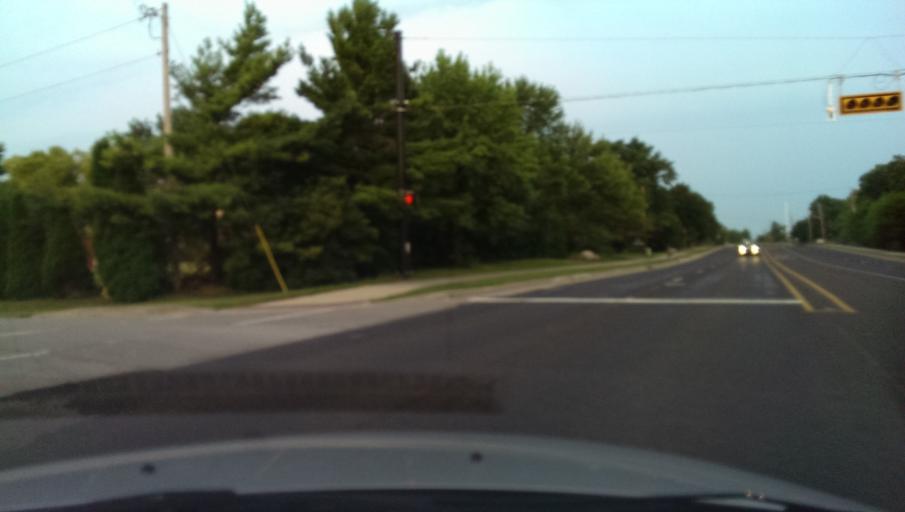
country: US
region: Indiana
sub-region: Hamilton County
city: Carmel
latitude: 40.0000
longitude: -86.1366
